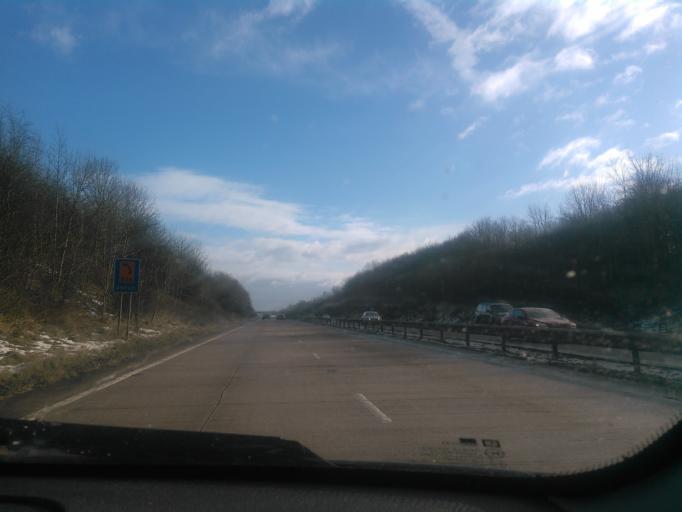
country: GB
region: England
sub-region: Staffordshire
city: Cheadle
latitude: 52.9421
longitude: -1.9995
